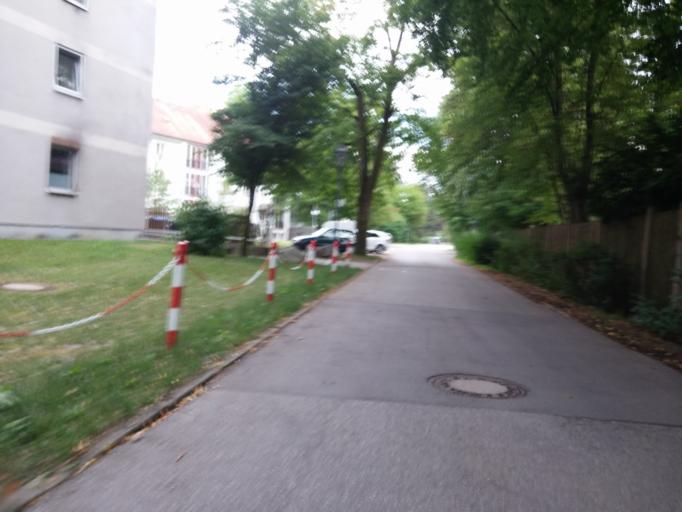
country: DE
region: Bavaria
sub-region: Upper Bavaria
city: Haar
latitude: 48.1187
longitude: 11.7440
